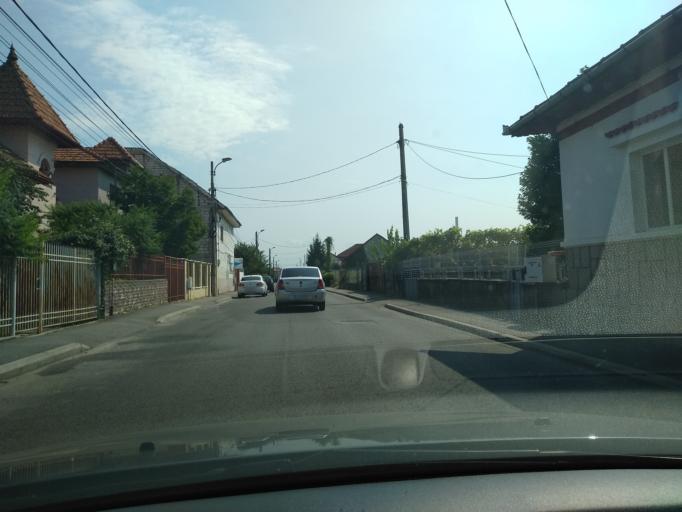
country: RO
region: Gorj
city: Targu Jiu
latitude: 45.0326
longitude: 23.2669
